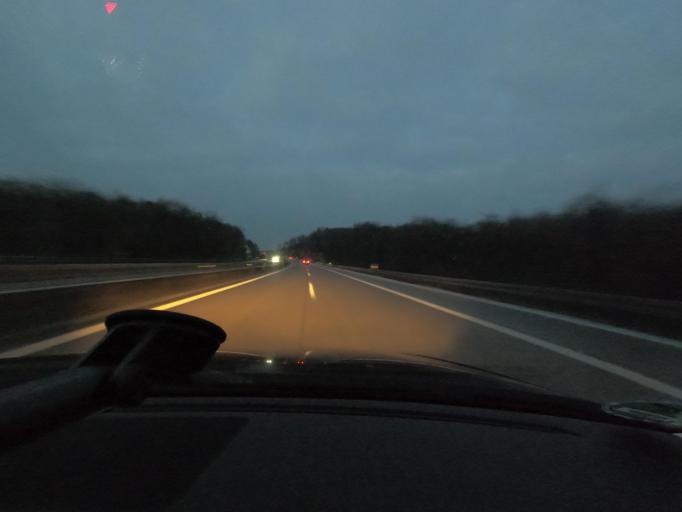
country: DE
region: Bavaria
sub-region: Upper Franconia
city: Meeder
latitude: 50.3638
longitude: 10.9215
